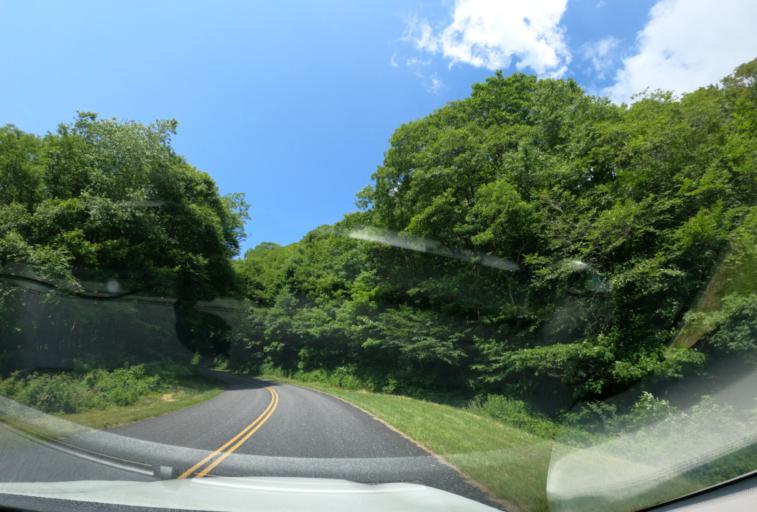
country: US
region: North Carolina
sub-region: Haywood County
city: Maggie Valley
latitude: 35.4525
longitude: -83.1039
